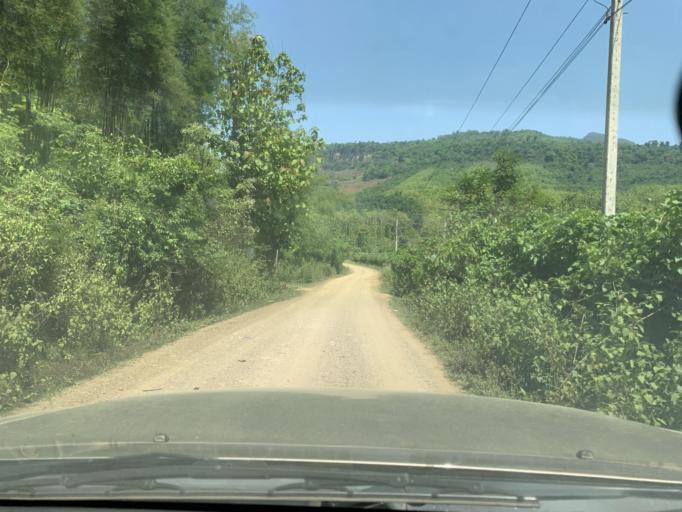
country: LA
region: Louangphabang
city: Louangphabang
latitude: 19.9139
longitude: 102.2636
